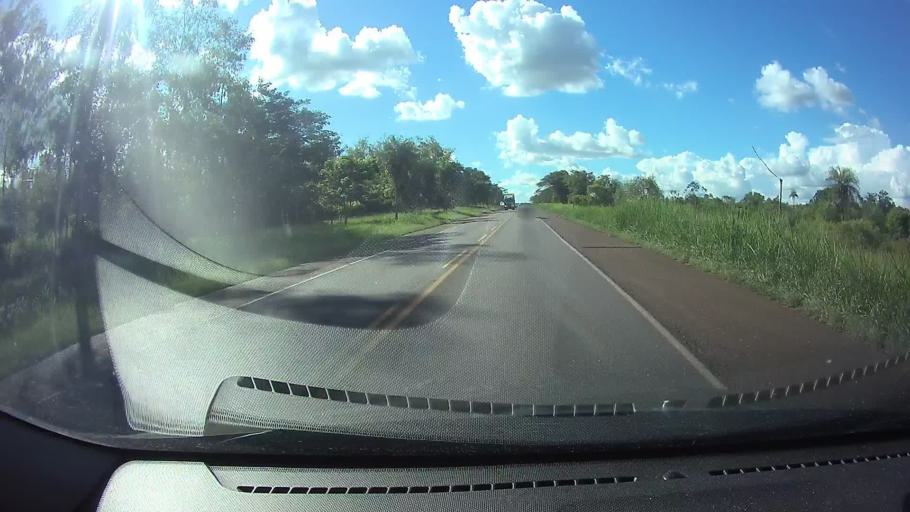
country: PY
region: Cordillera
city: Itacurubi de la Cordillera
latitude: -25.4345
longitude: -56.9113
